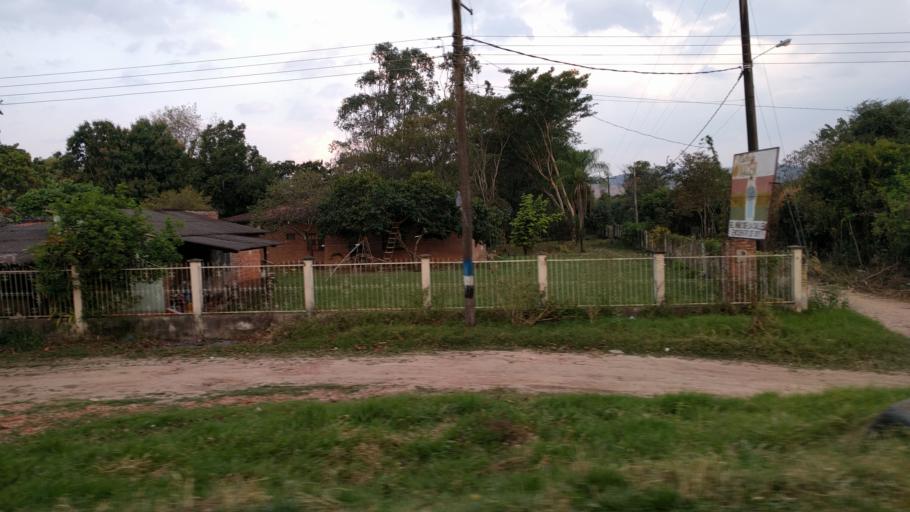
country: BO
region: Santa Cruz
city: Jorochito
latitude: -18.1272
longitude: -63.4667
